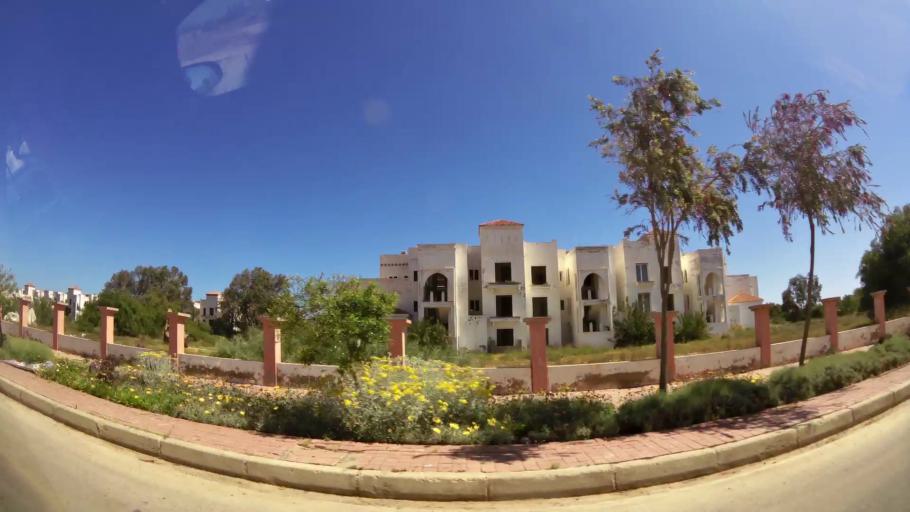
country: MA
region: Oriental
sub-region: Berkane-Taourirt
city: Madagh
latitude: 35.1099
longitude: -2.3152
